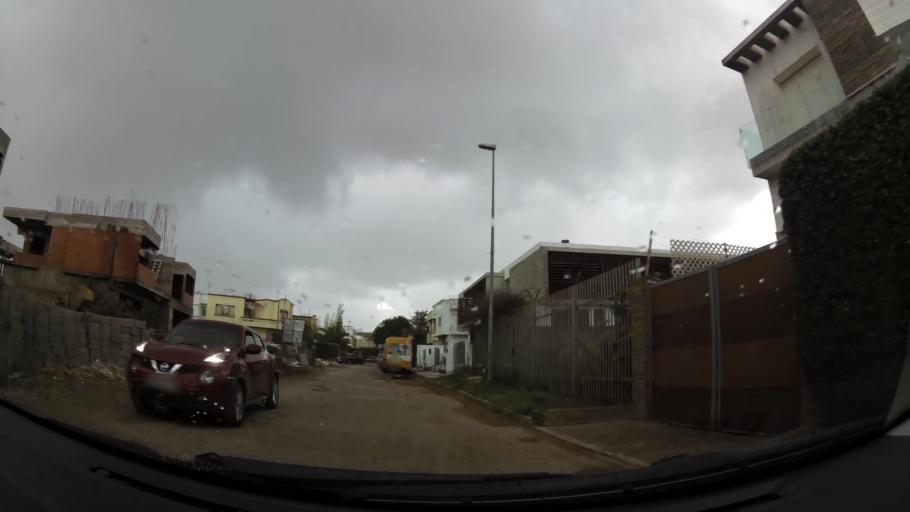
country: MA
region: Grand Casablanca
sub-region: Casablanca
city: Casablanca
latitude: 33.5747
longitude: -7.6833
